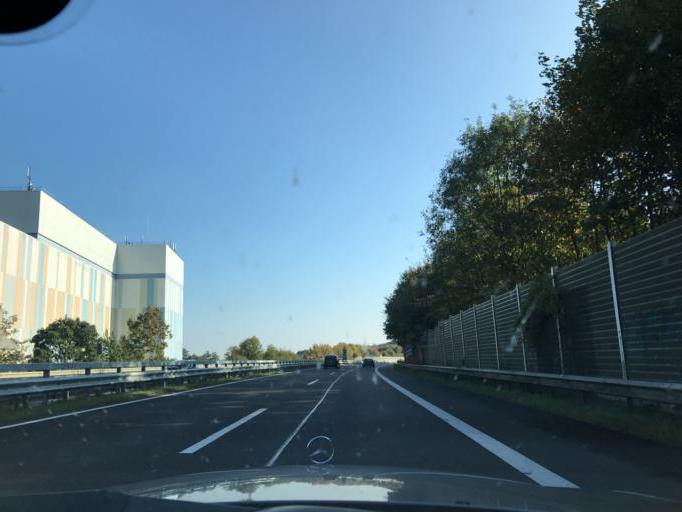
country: DE
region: Lower Saxony
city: Westerstede
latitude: 53.2639
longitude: 7.9361
